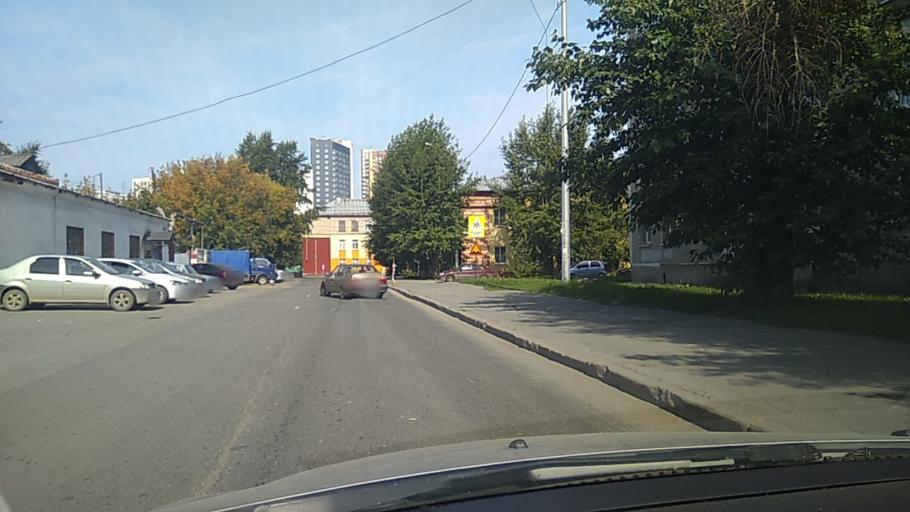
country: RU
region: Sverdlovsk
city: Yekaterinburg
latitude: 56.8002
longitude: 60.6334
